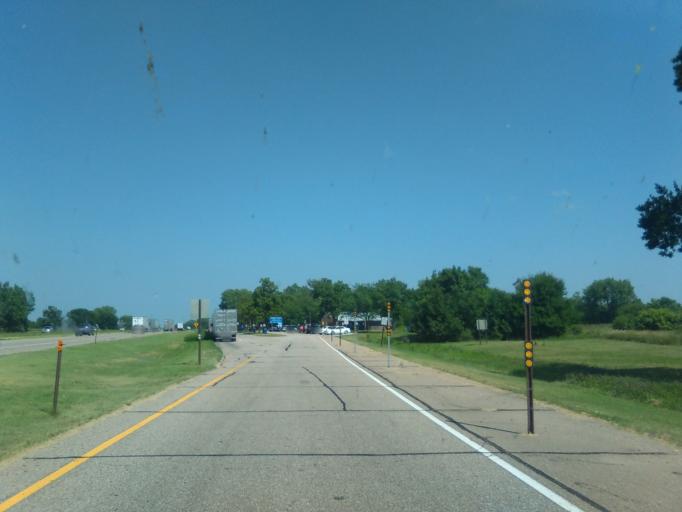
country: US
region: Nebraska
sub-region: Buffalo County
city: Kearney
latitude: 40.6709
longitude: -99.1593
